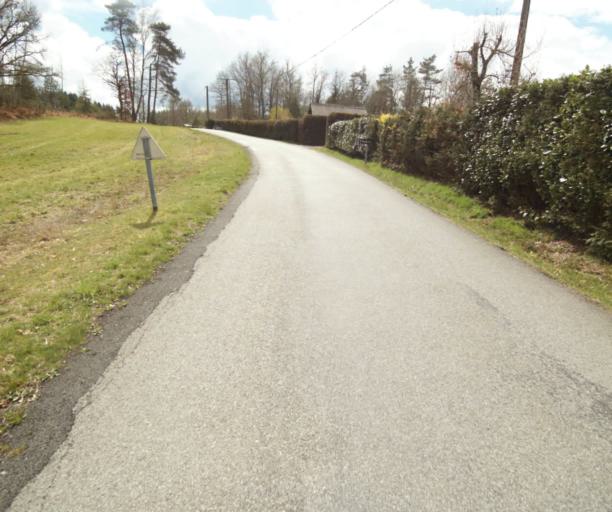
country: FR
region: Limousin
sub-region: Departement de la Correze
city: Correze
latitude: 45.3279
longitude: 1.9168
